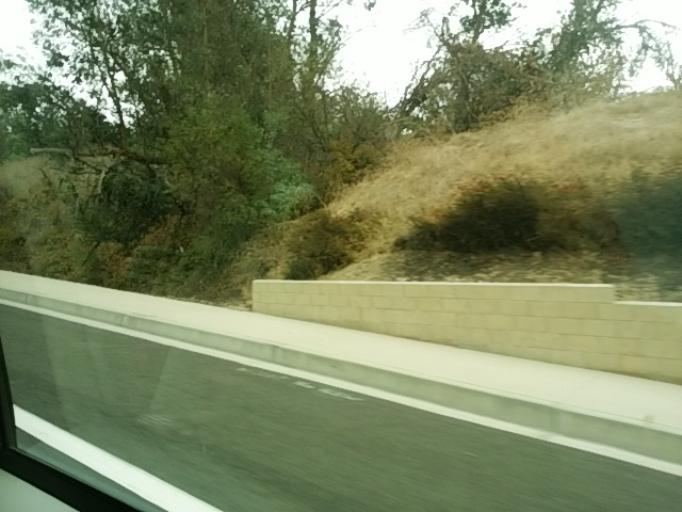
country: US
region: California
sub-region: Orange County
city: North Tustin
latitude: 33.7777
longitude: -117.7775
